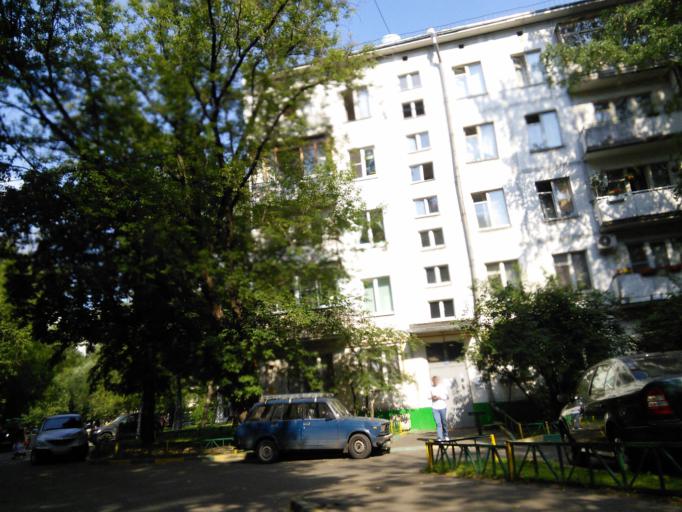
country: RU
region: Moskovskaya
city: Bogorodskoye
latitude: 55.7965
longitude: 37.7245
